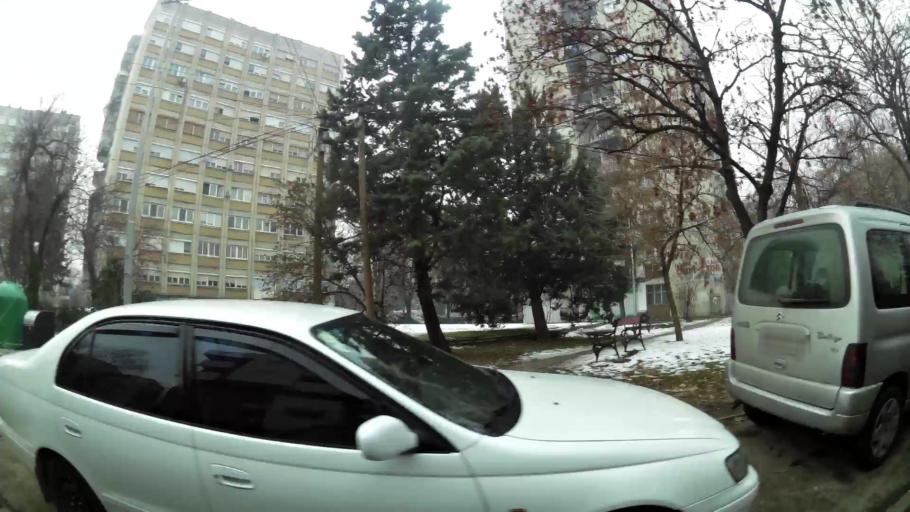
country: MK
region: Cair
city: Cair
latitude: 42.0028
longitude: 21.4621
